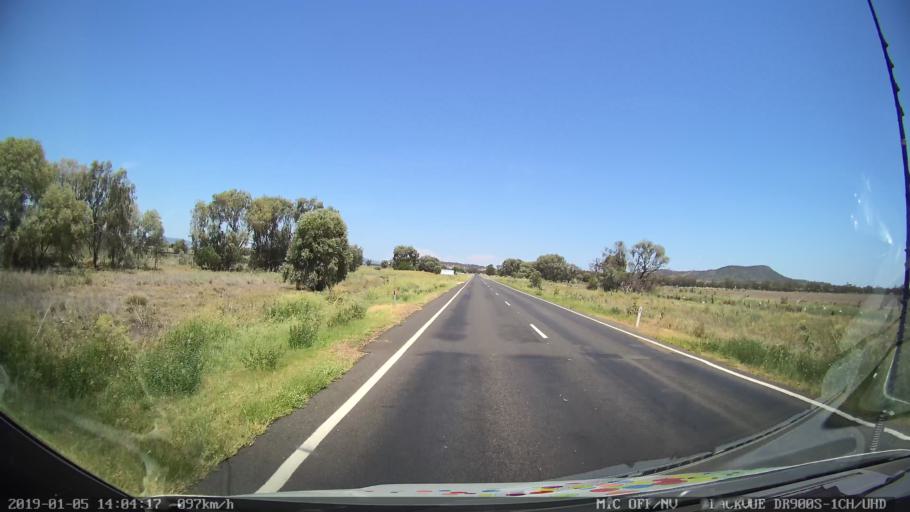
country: AU
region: New South Wales
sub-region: Gunnedah
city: Gunnedah
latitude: -31.1984
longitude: 150.3619
